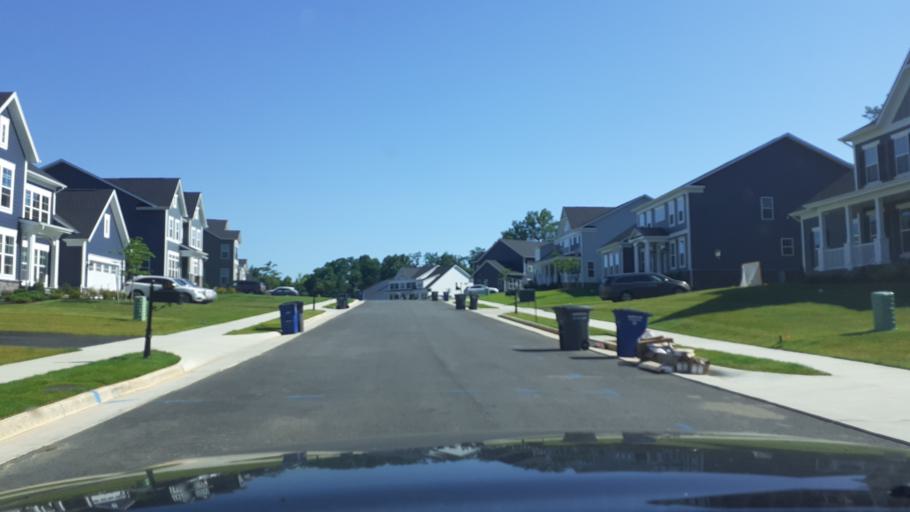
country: US
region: Virginia
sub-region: Fairfax County
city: Mantua
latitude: 38.8626
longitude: -77.2543
